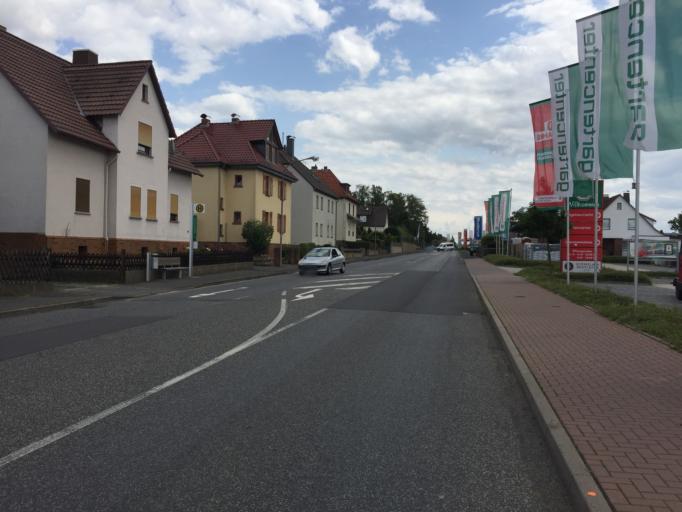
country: DE
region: Hesse
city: Schwalmstadt
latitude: 50.9191
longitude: 9.2027
